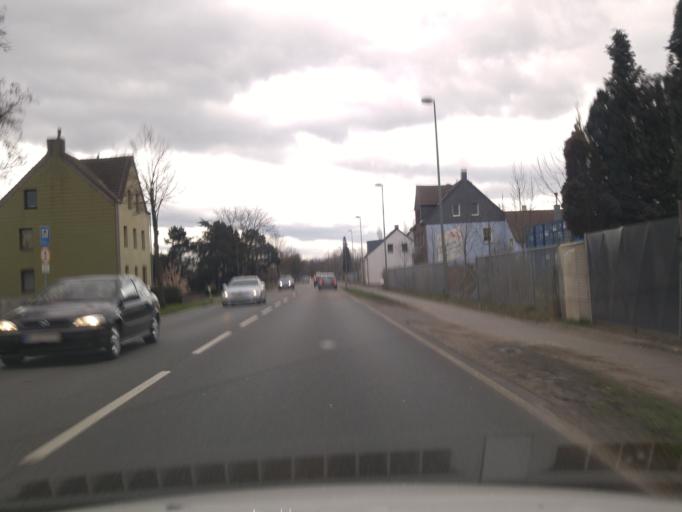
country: DE
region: North Rhine-Westphalia
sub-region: Regierungsbezirk Dusseldorf
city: Dusseldorf
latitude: 51.1570
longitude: 6.7798
